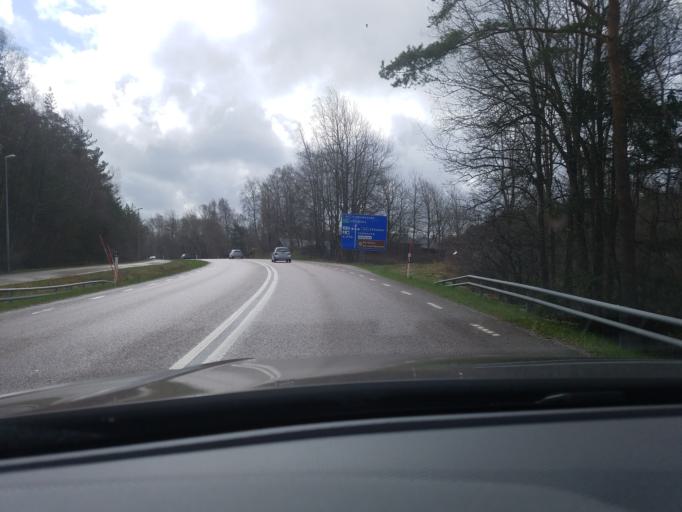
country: SE
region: Vaestra Goetaland
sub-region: Tjorns Kommun
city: Myggenas
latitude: 58.0595
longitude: 11.7552
